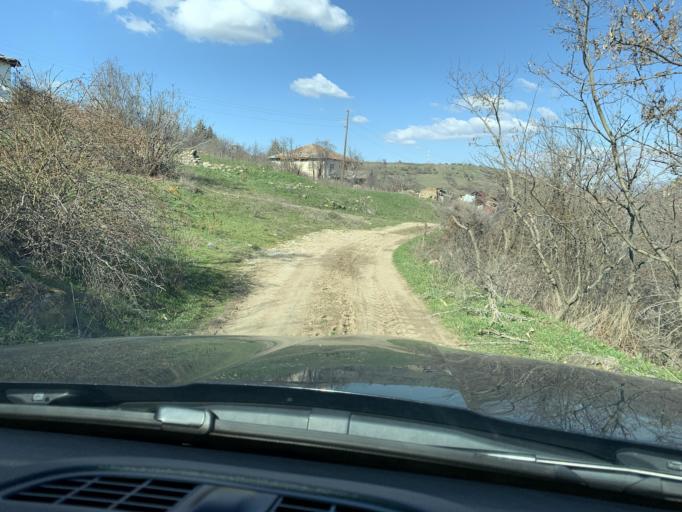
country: MK
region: Demir Kapija
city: Demir Kapija
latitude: 41.4169
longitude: 22.1664
